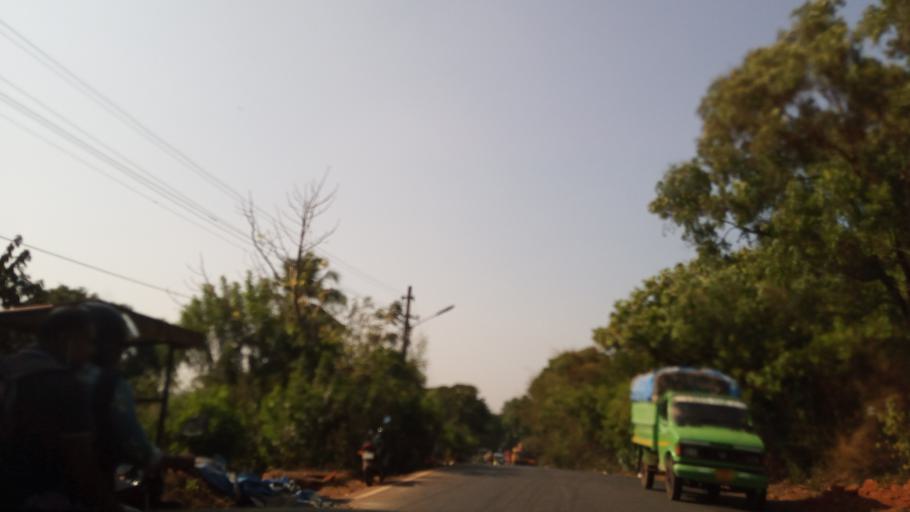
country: IN
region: Goa
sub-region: North Goa
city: Jua
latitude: 15.4811
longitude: 73.9602
